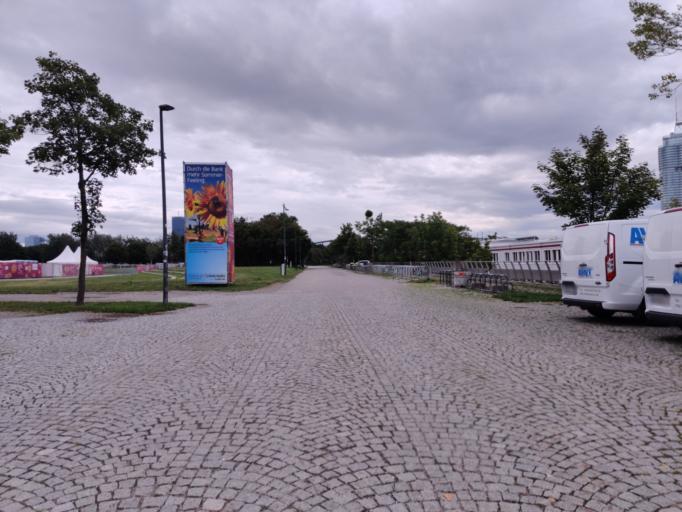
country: AT
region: Vienna
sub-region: Wien Stadt
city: Vienna
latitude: 48.2468
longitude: 16.3874
